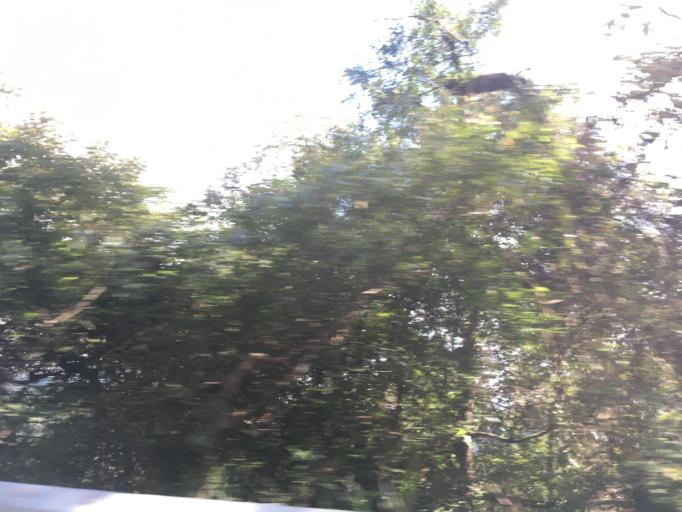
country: TW
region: Taiwan
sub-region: Yilan
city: Yilan
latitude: 24.7505
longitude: 121.6437
